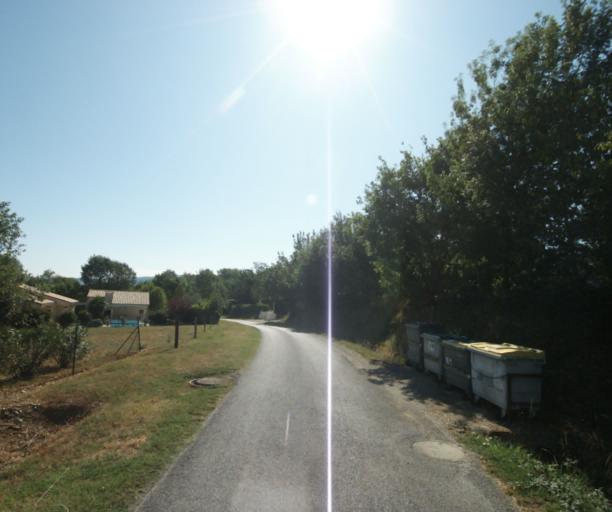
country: FR
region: Midi-Pyrenees
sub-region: Departement de la Haute-Garonne
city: Revel
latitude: 43.4475
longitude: 2.0173
